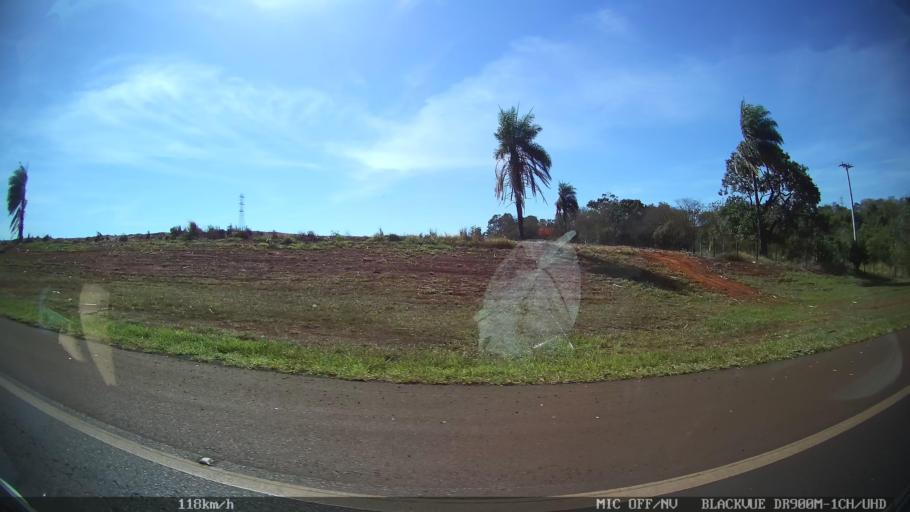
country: BR
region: Sao Paulo
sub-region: Ipua
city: Ipua
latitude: -20.4598
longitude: -48.1459
